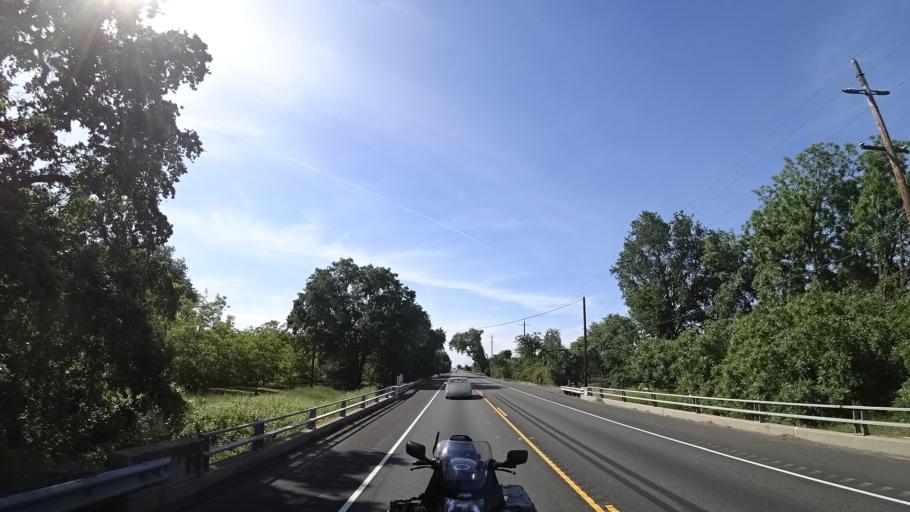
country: US
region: California
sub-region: Glenn County
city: Hamilton City
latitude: 39.8807
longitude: -121.9729
